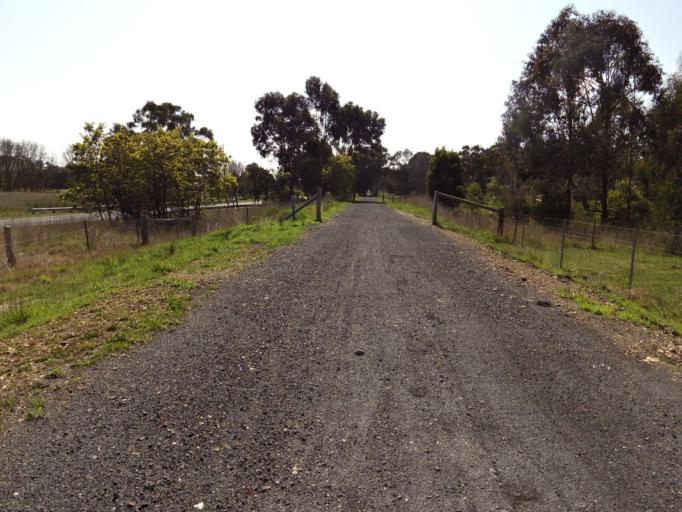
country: AU
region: Victoria
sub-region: Murrindindi
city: Alexandra
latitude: -37.1298
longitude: 145.5952
